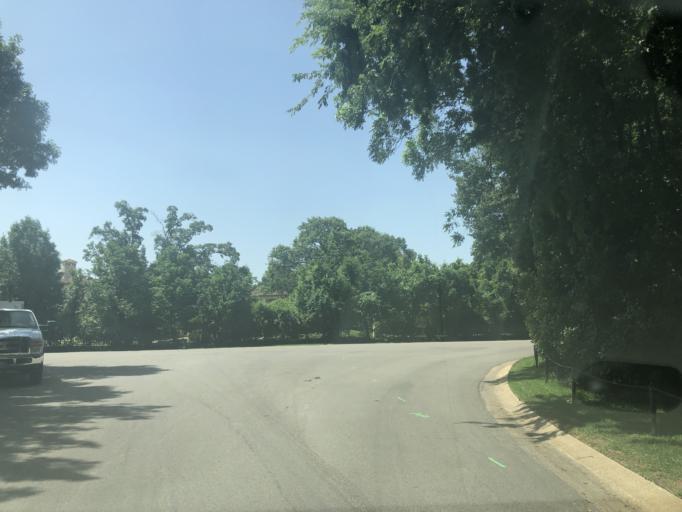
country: US
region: Texas
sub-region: Dallas County
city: University Park
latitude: 32.8797
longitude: -96.8288
